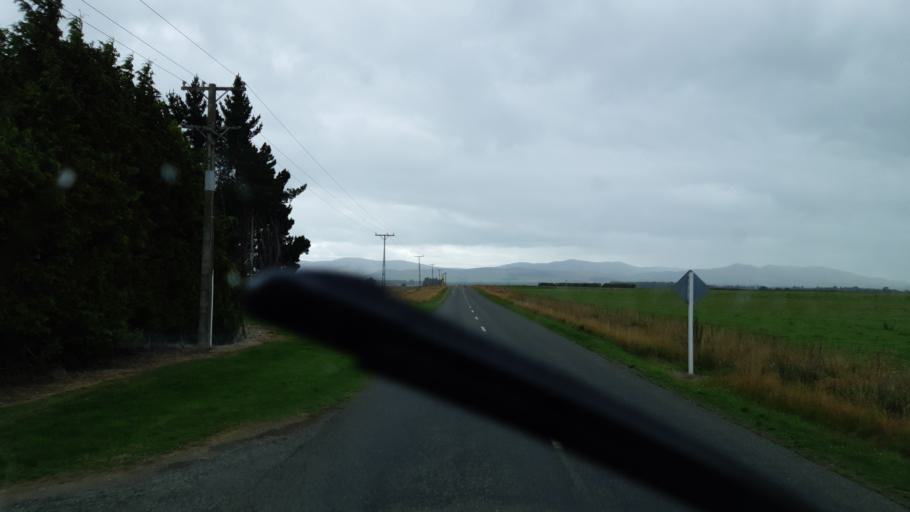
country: NZ
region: Southland
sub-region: Southland District
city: Winton
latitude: -45.7627
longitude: 168.4932
